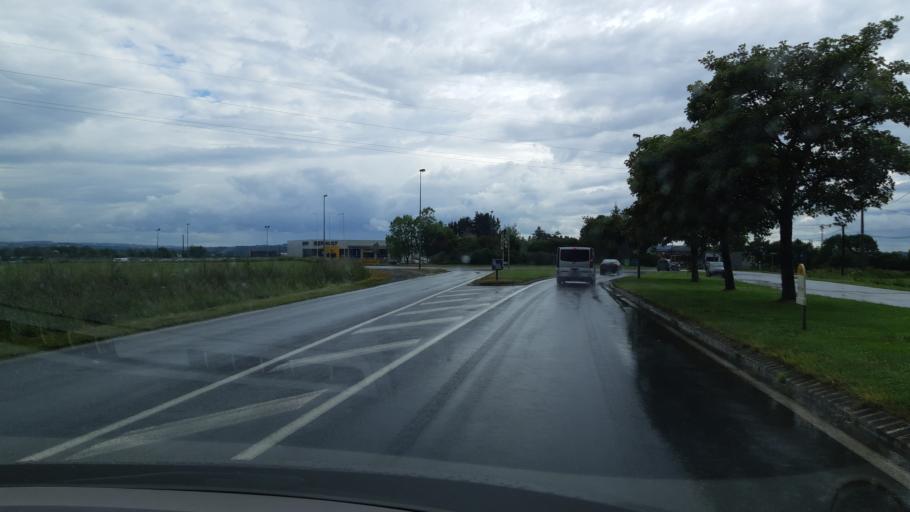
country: FR
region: Brittany
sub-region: Departement du Finistere
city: Landivisiau
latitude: 48.5278
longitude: -4.0663
